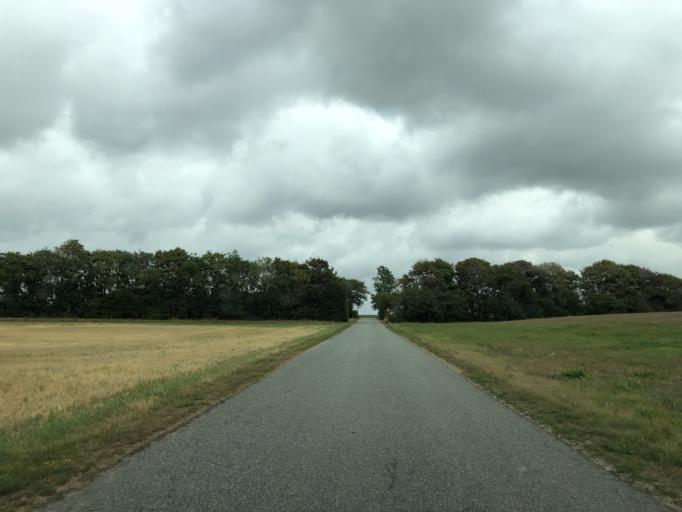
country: DK
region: Central Jutland
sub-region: Ringkobing-Skjern Kommune
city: Videbaek
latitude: 56.1062
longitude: 8.4951
